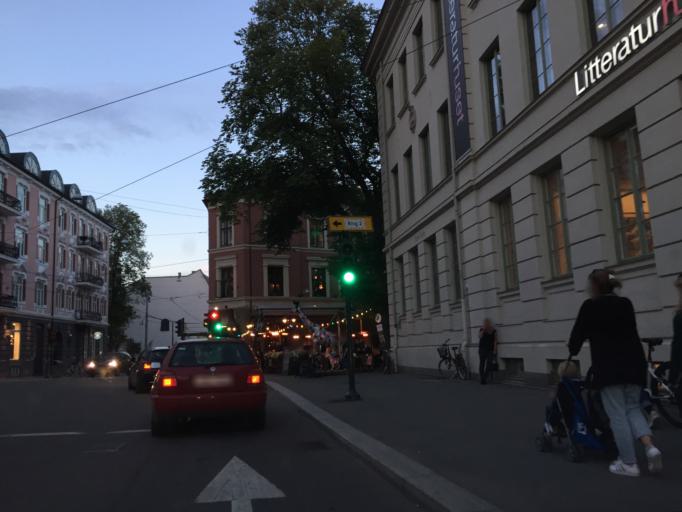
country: NO
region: Oslo
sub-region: Oslo
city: Oslo
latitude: 59.9204
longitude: 10.7283
